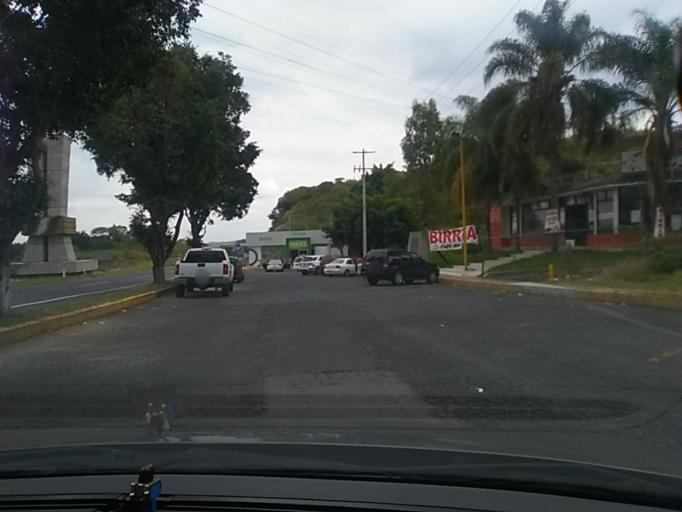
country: MX
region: Jalisco
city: Ocotlan
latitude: 20.4045
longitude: -102.7378
